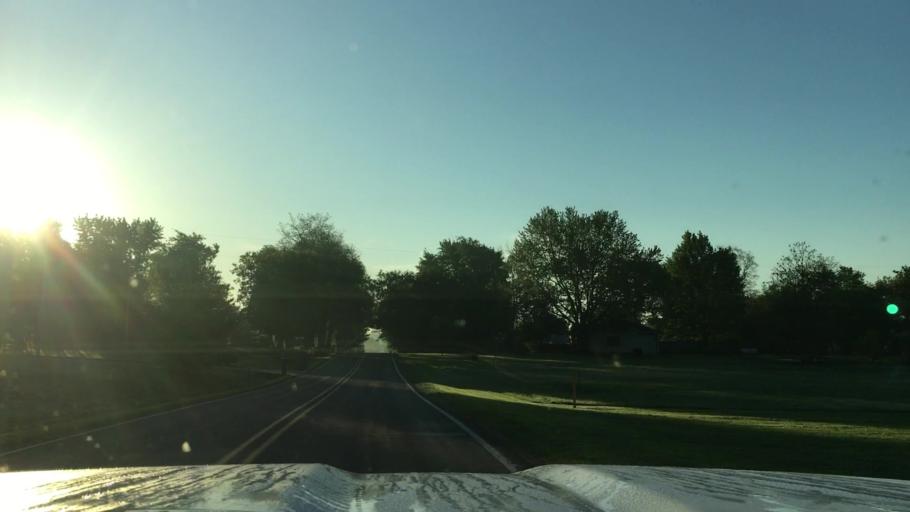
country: US
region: Michigan
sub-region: Kent County
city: Byron Center
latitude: 42.7828
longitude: -85.7593
